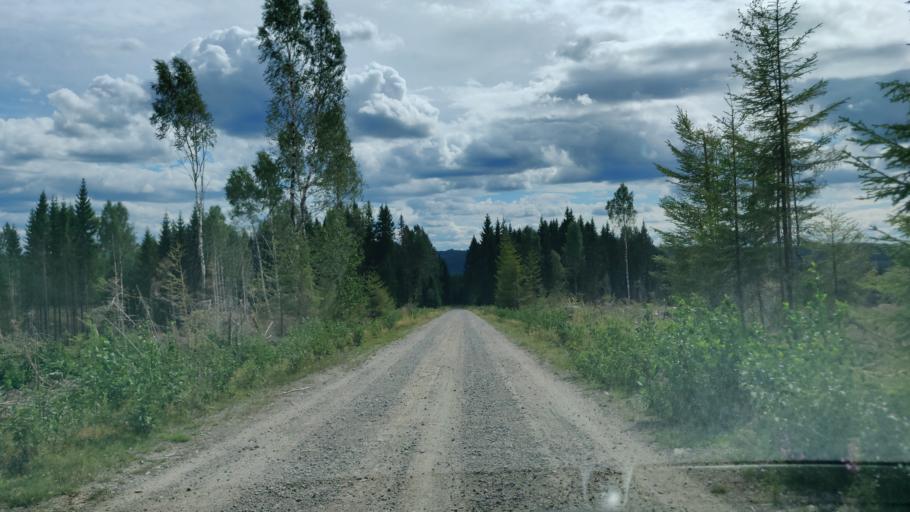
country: SE
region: Vaermland
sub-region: Hagfors Kommun
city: Hagfors
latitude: 60.0081
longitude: 13.7273
